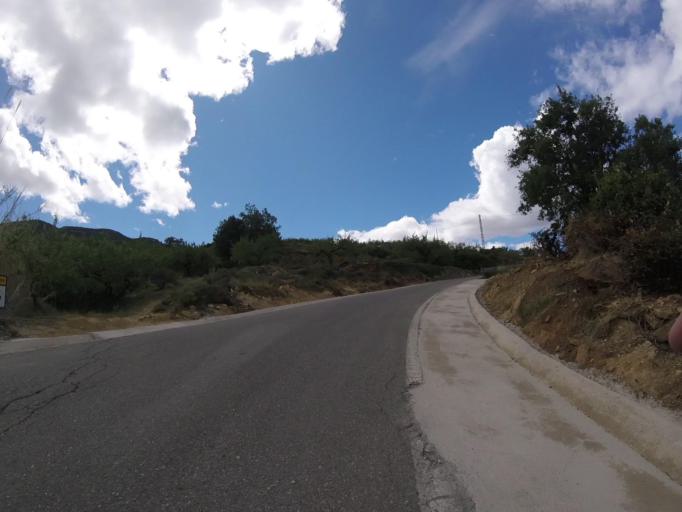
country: ES
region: Valencia
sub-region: Provincia de Castello
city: Sierra-Engarceran
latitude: 40.2954
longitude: -0.0408
